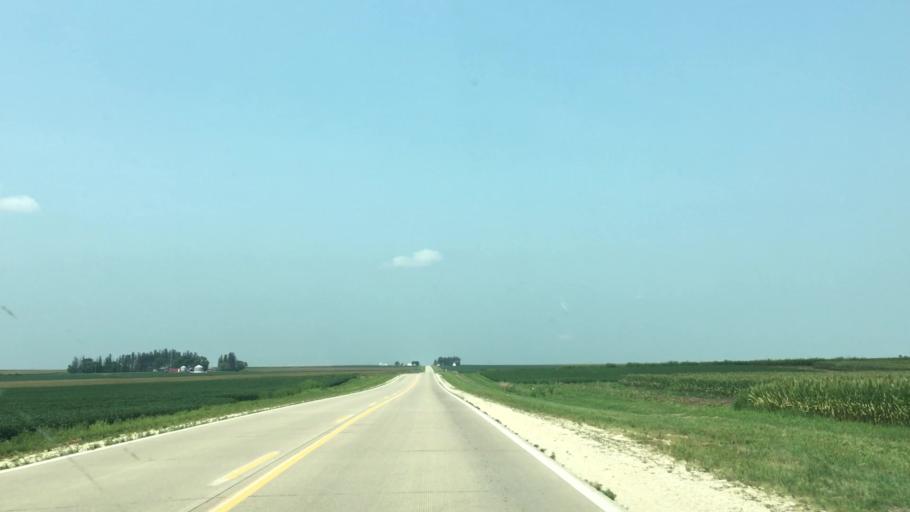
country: US
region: Iowa
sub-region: Fayette County
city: Oelwein
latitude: 42.6926
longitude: -91.8051
